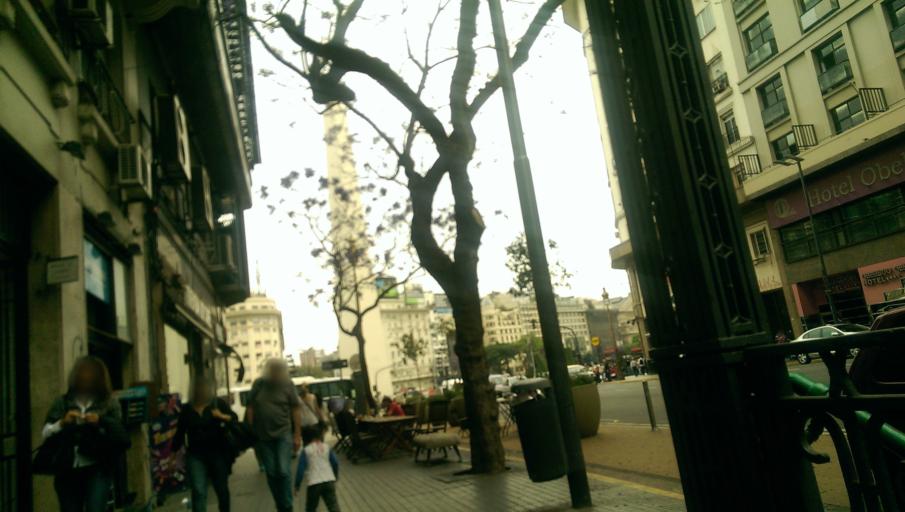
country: AR
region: Buenos Aires F.D.
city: Buenos Aires
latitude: -34.6043
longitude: -58.3805
